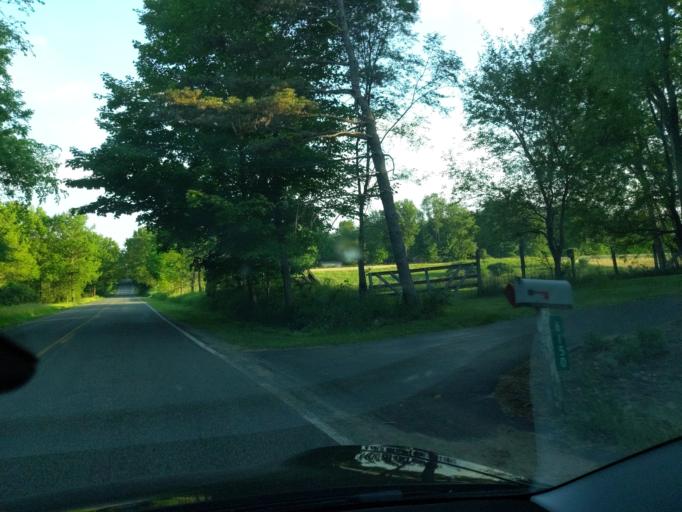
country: US
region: Michigan
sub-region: Barry County
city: Nashville
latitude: 42.5650
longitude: -85.0941
